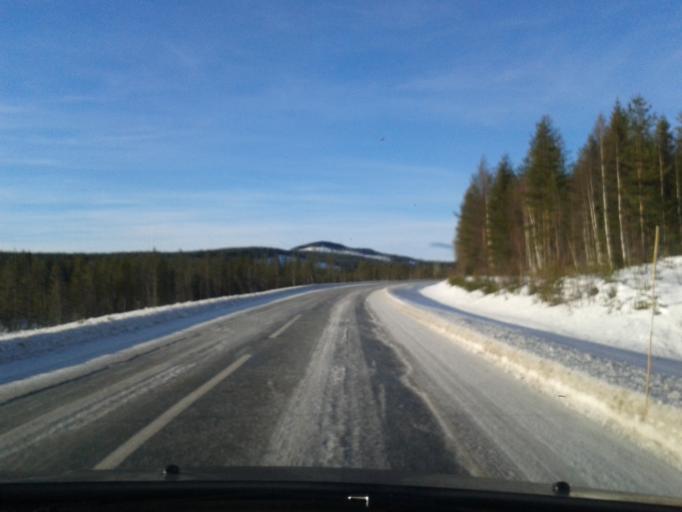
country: SE
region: Vaesternorrland
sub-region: OErnskoeldsviks Kommun
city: Bredbyn
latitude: 63.7539
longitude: 17.7068
